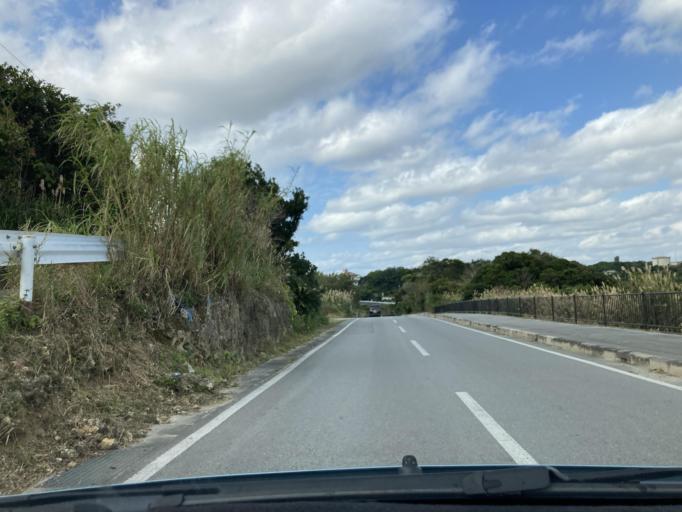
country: JP
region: Okinawa
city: Tomigusuku
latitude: 26.1797
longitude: 127.7604
